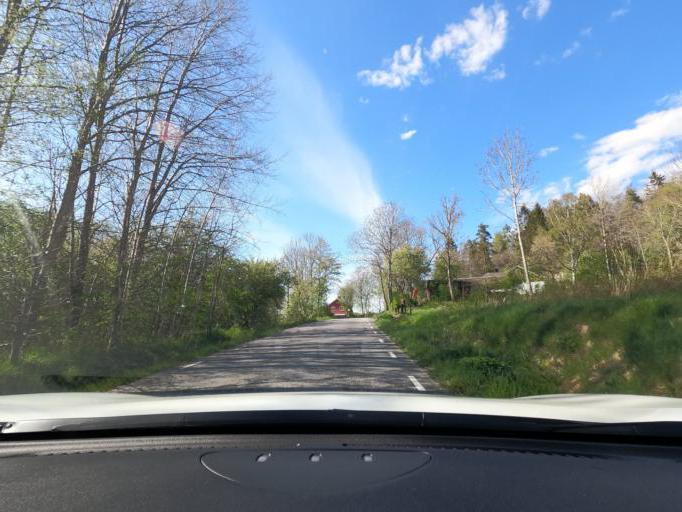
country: SE
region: Vaestra Goetaland
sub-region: Harryda Kommun
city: Ravlanda
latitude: 57.6312
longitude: 12.4983
